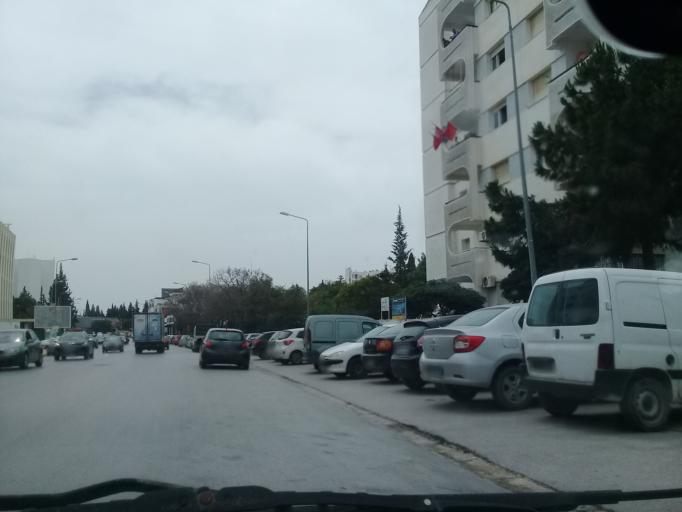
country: TN
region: Tunis
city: Tunis
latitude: 36.8375
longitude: 10.1578
